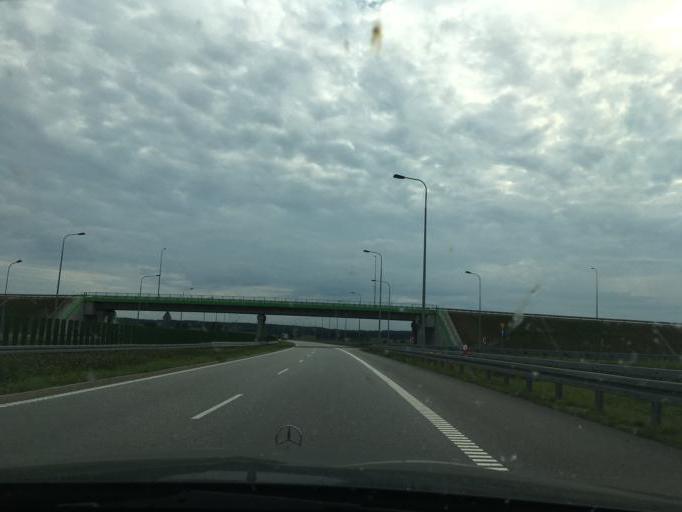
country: PL
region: Podlasie
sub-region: Powiat kolnenski
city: Stawiski
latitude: 53.3877
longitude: 22.1449
